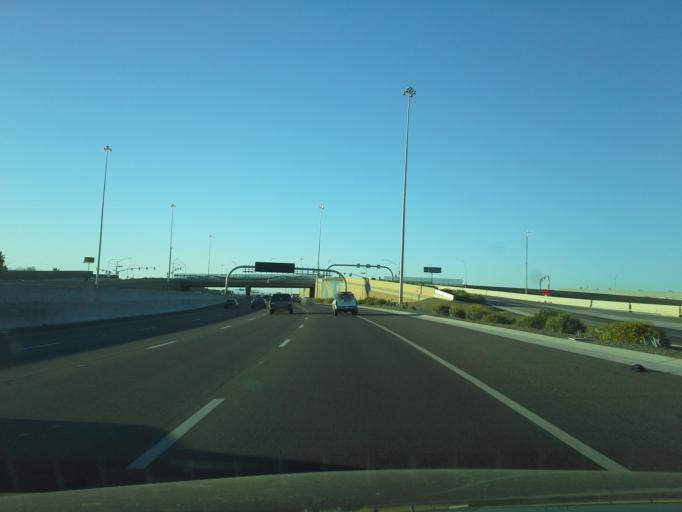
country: US
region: Arizona
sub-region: Pima County
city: Flowing Wells
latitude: 32.2696
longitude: -111.0086
